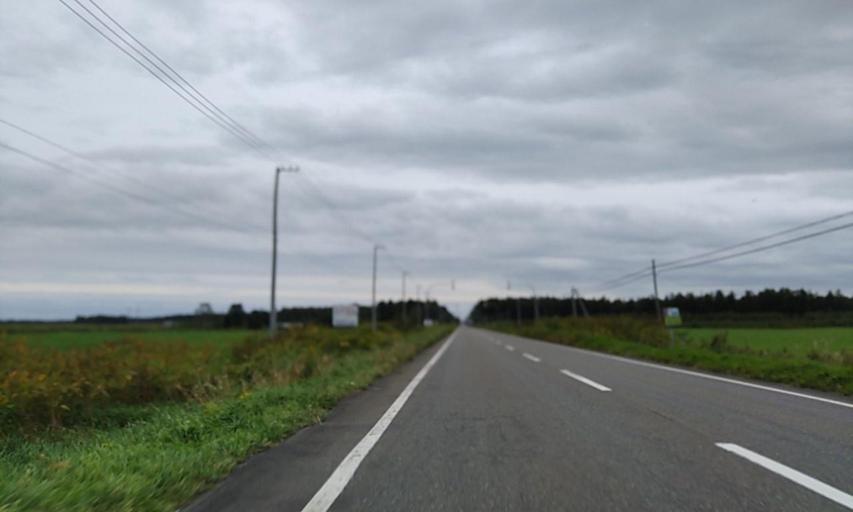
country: JP
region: Hokkaido
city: Obihiro
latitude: 42.3389
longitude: 143.3064
